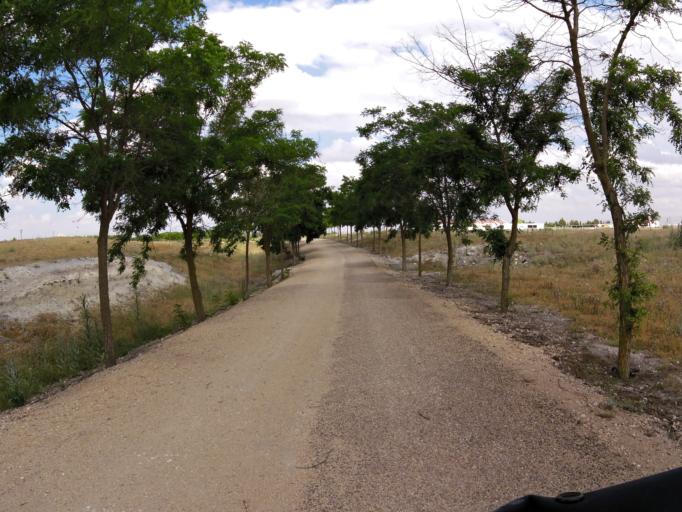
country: ES
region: Castille-La Mancha
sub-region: Provincia de Albacete
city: Albacete
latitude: 38.9609
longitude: -1.9643
